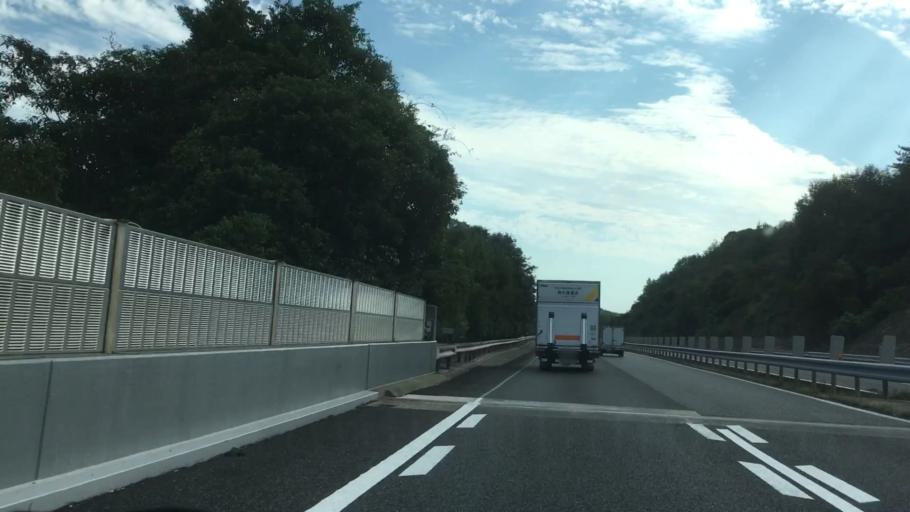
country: JP
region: Hiroshima
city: Ono-hara
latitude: 34.3121
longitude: 132.2805
